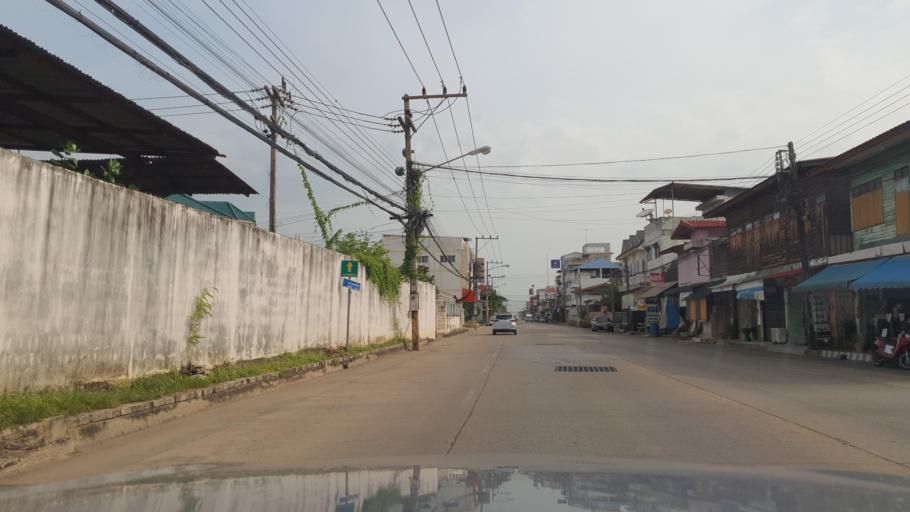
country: TH
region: Phitsanulok
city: Phitsanulok
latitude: 16.8334
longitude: 100.2655
